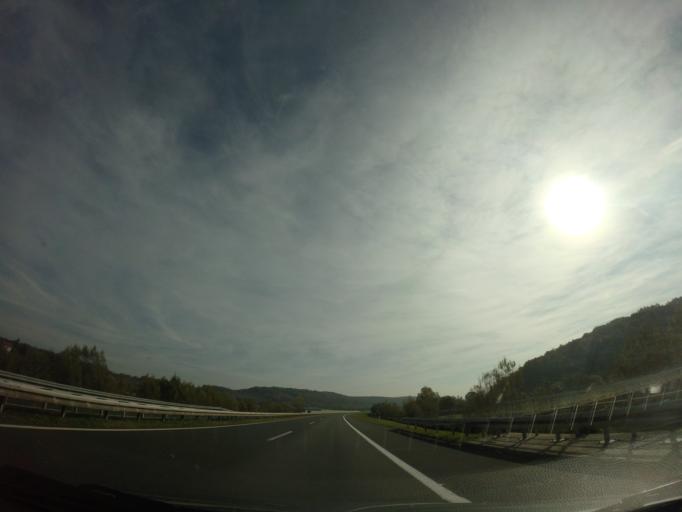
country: HR
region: Varazdinska
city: Remetinec
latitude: 46.0768
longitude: 16.2931
